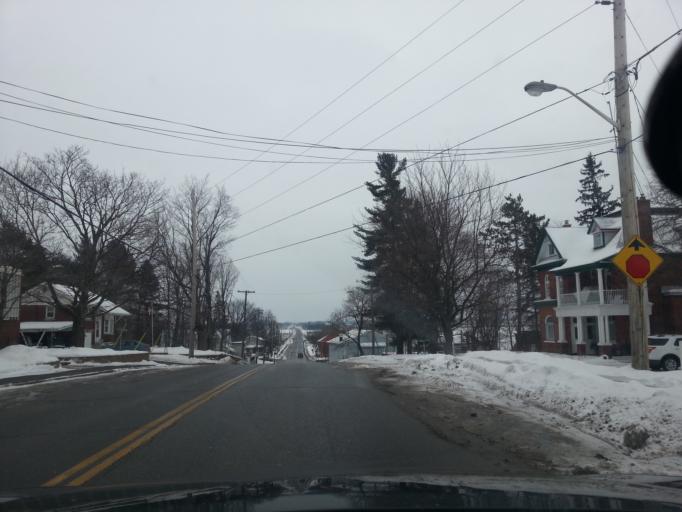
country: CA
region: Ontario
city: Bells Corners
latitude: 45.3456
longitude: -76.0372
